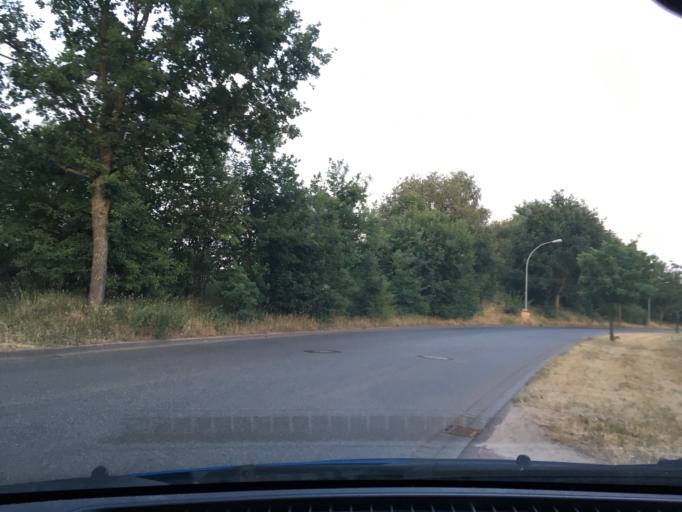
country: DE
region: Lower Saxony
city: Emmendorf
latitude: 52.9947
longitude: 10.5474
